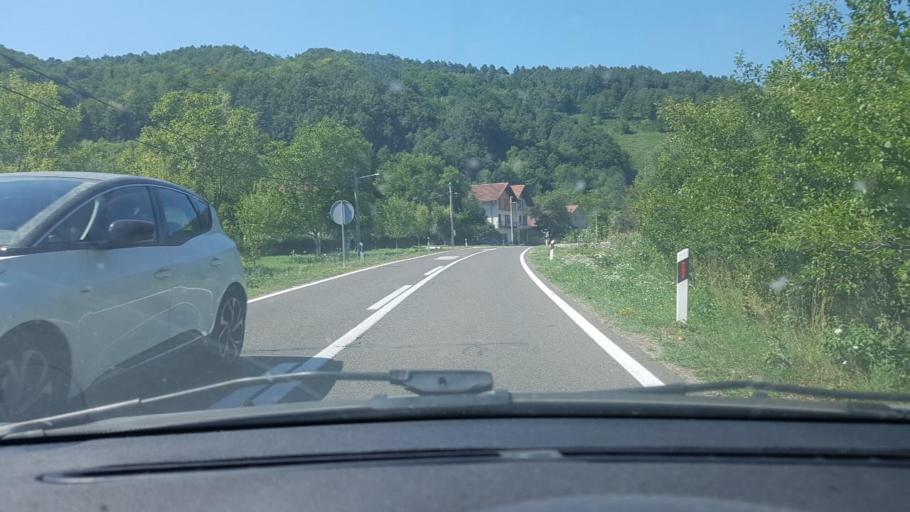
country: BA
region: Federation of Bosnia and Herzegovina
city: Bihac
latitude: 44.7404
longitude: 15.9201
